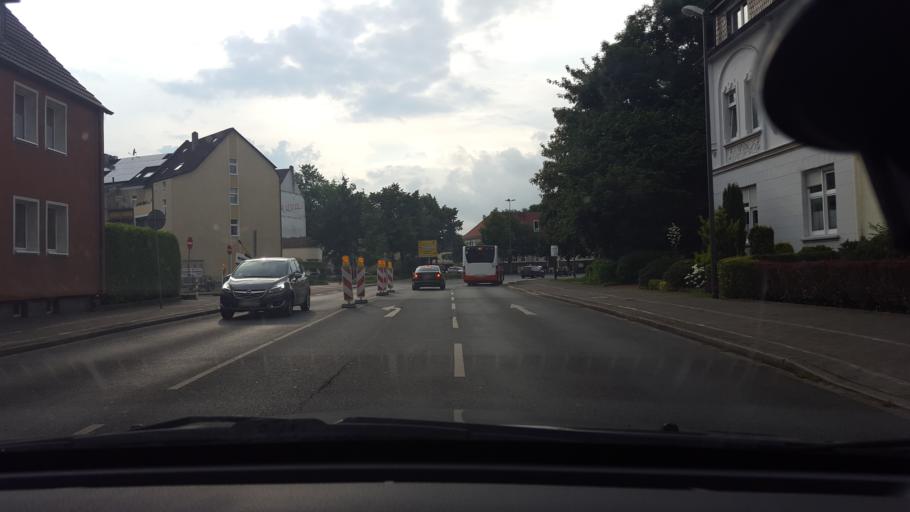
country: DE
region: North Rhine-Westphalia
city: Herten
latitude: 51.6000
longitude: 7.0939
